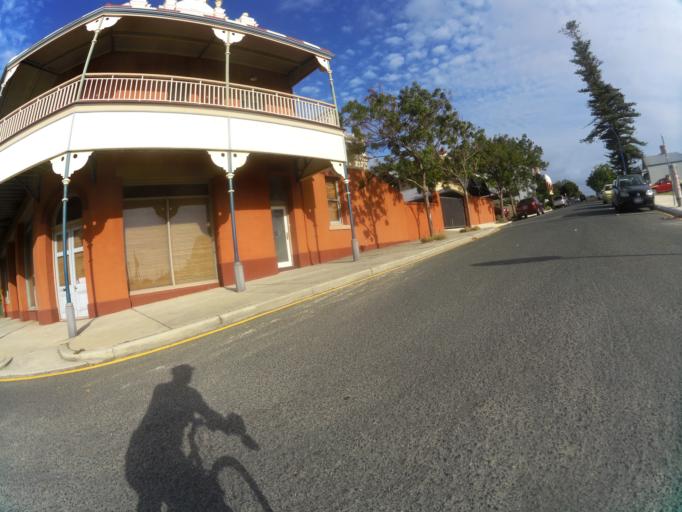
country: AU
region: Western Australia
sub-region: East Fremantle
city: East Fremantle
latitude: -32.0419
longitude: 115.7592
